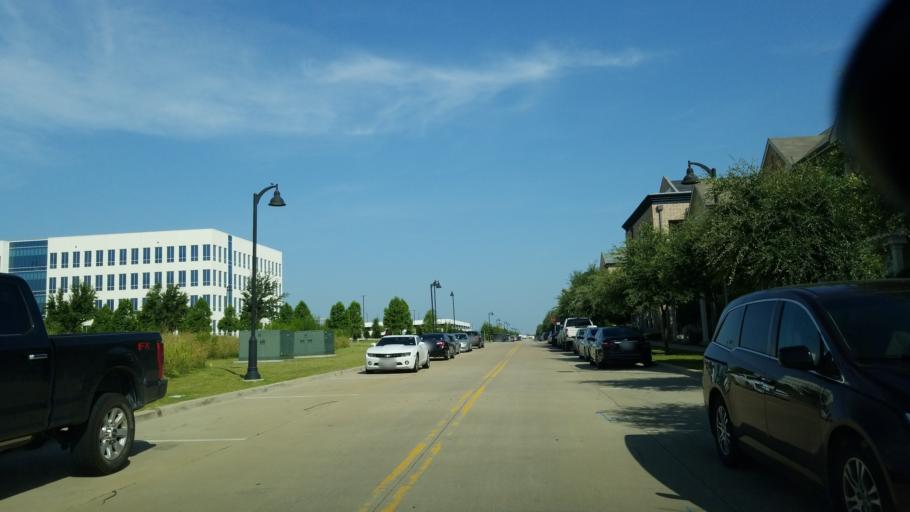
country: US
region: Texas
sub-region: Dallas County
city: Coppell
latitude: 32.9309
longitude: -96.9850
